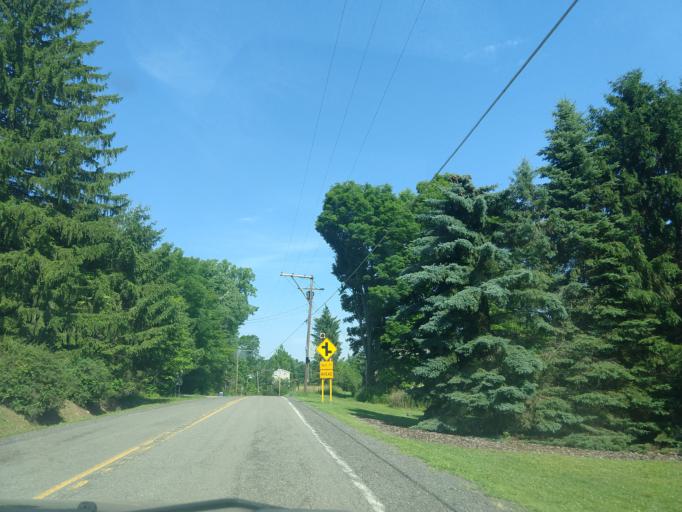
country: US
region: New York
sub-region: Tompkins County
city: East Ithaca
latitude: 42.4027
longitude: -76.4621
